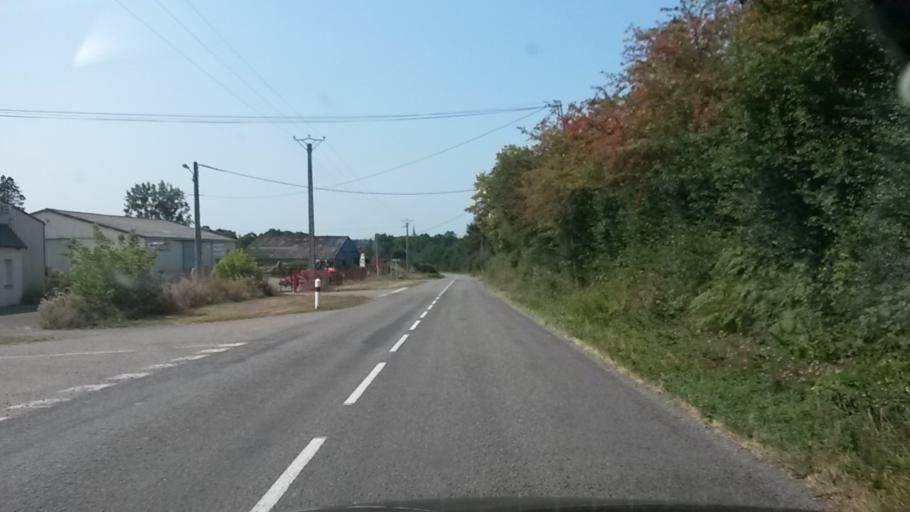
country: FR
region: Pays de la Loire
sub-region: Departement de la Mayenne
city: Saint-Pierre-des-Nids
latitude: 48.4055
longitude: -0.0809
